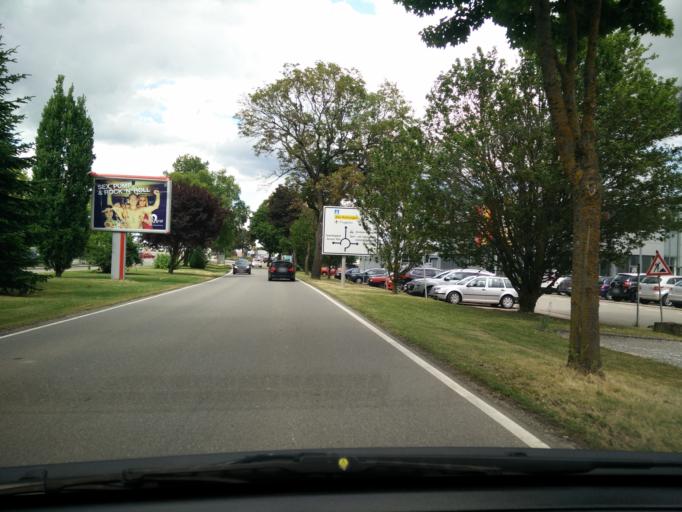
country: DE
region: Baden-Wuerttemberg
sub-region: Freiburg Region
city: Donaueschingen
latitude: 47.9616
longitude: 8.5045
